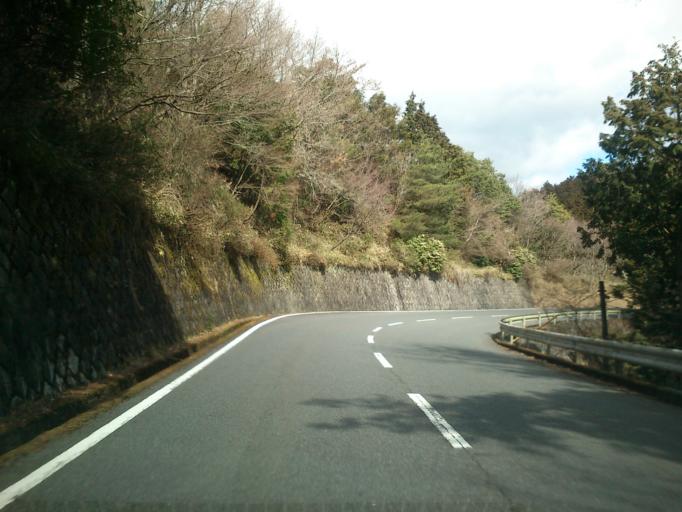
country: JP
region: Shiga Prefecture
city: Otsu-shi
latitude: 35.0397
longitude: 135.8380
